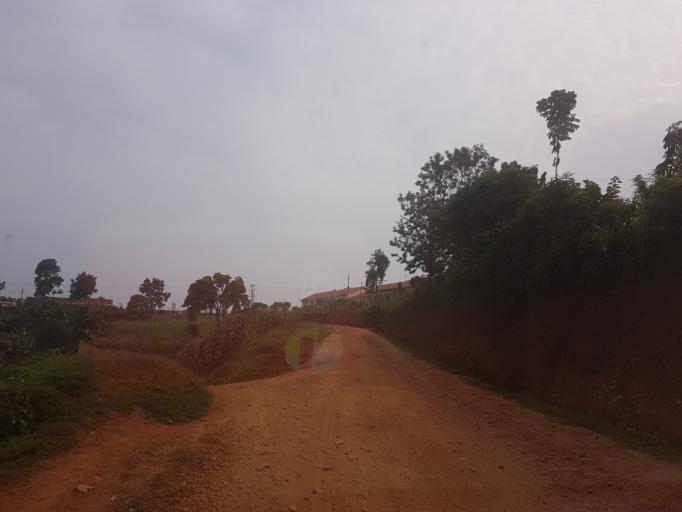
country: UG
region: Western Region
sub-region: Kanungu District
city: Kanungu
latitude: -0.8959
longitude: 29.7776
